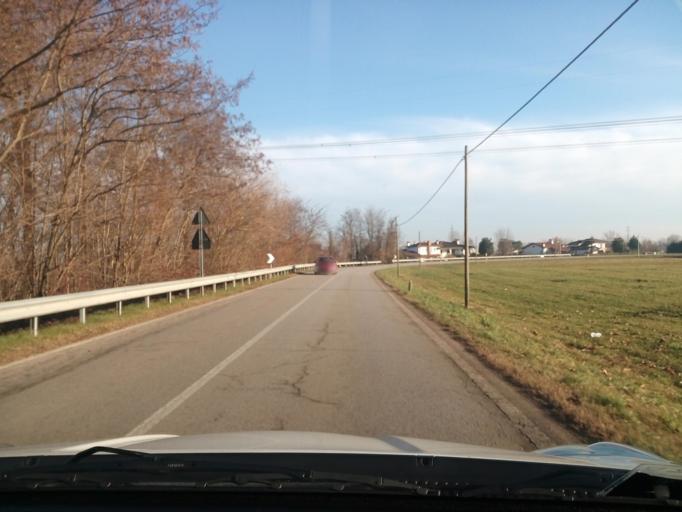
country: IT
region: Veneto
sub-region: Provincia di Vicenza
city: Novoledo
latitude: 45.6442
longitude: 11.5230
